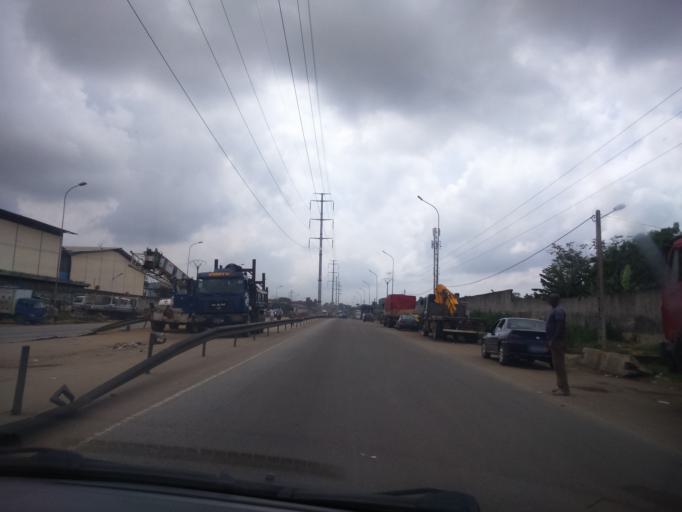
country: CI
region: Lagunes
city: Abobo
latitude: 5.3706
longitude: -4.0796
